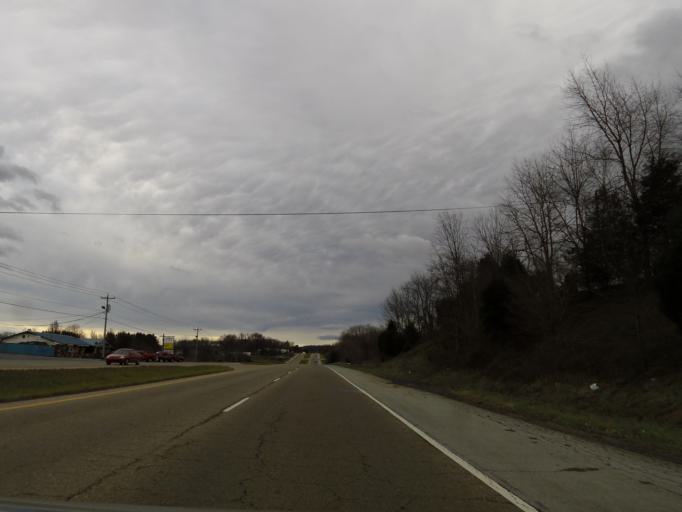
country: US
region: Tennessee
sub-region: Washington County
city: Jonesborough
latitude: 36.2553
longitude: -82.5878
